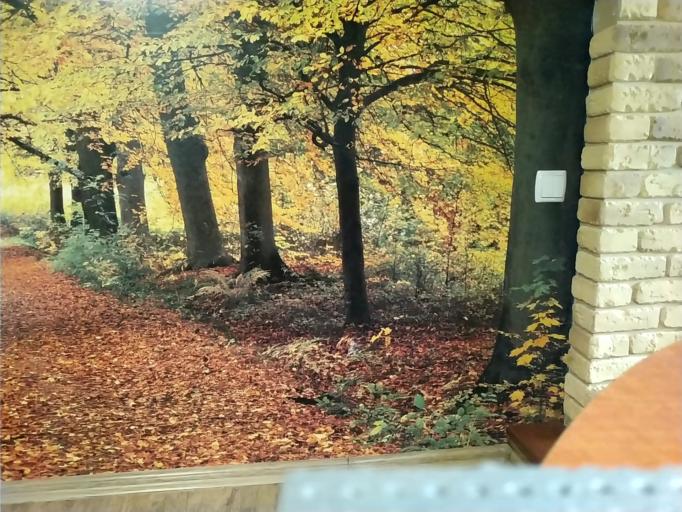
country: RU
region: Tverskaya
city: Kalashnikovo
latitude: 57.2710
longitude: 35.1813
